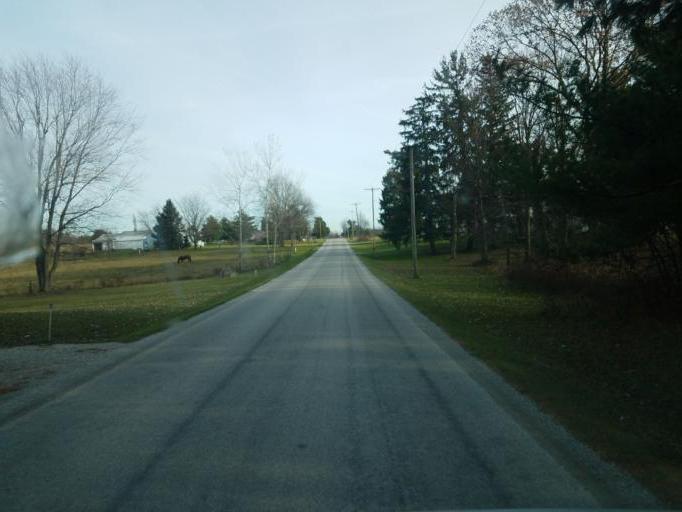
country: US
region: Ohio
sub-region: Morrow County
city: Mount Gilead
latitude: 40.5783
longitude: -82.7278
